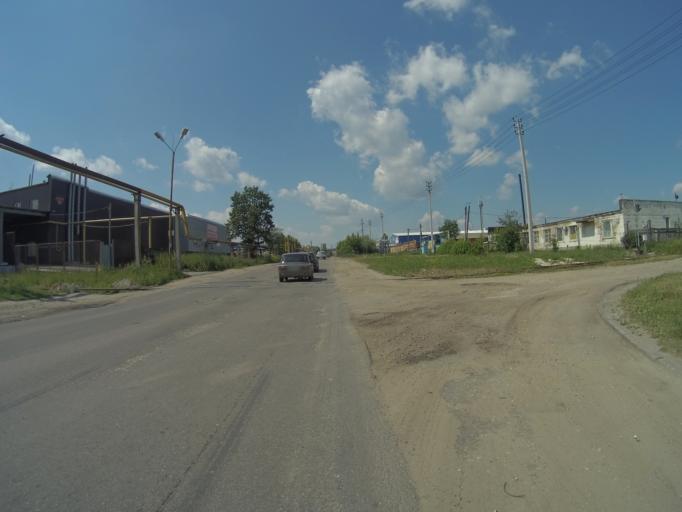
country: RU
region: Vladimir
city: Vladimir
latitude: 56.0939
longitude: 40.3563
